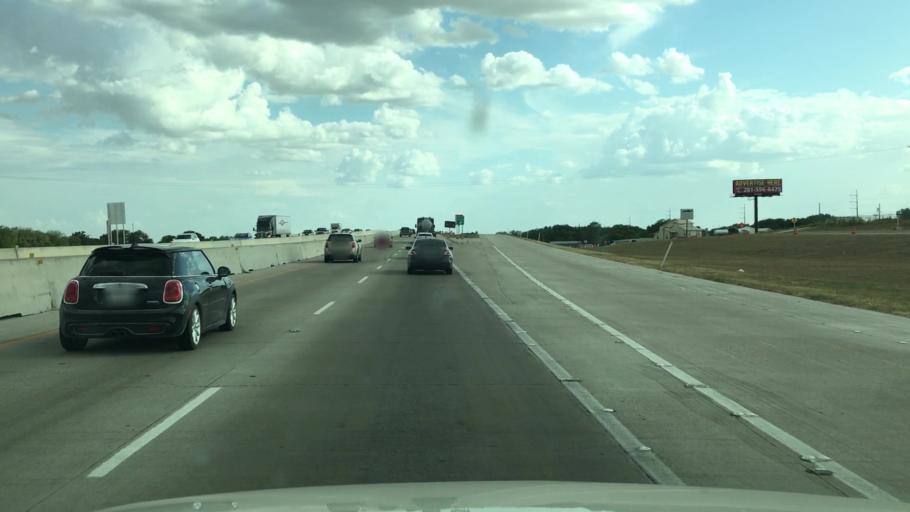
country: US
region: Texas
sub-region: Bell County
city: Troy
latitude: 31.1821
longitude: -97.3137
